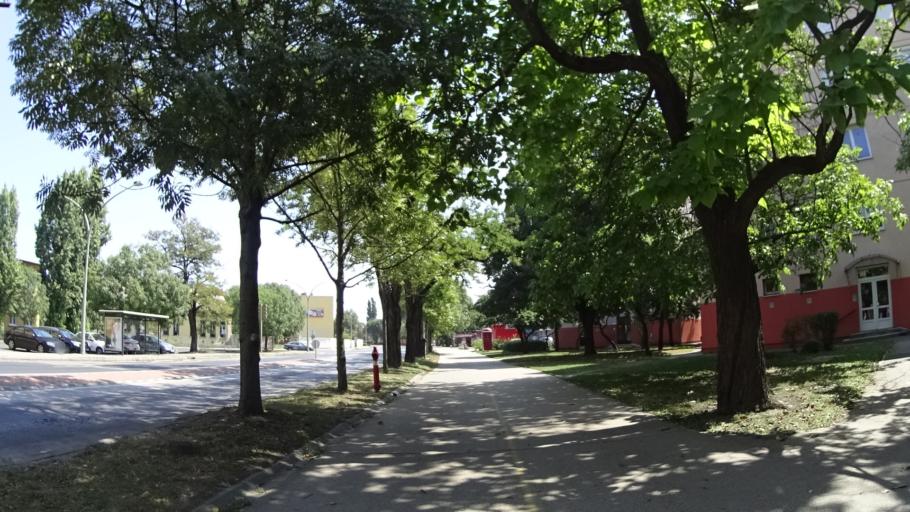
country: HU
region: Fejer
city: Szekesfehervar
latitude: 47.1834
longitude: 18.4190
